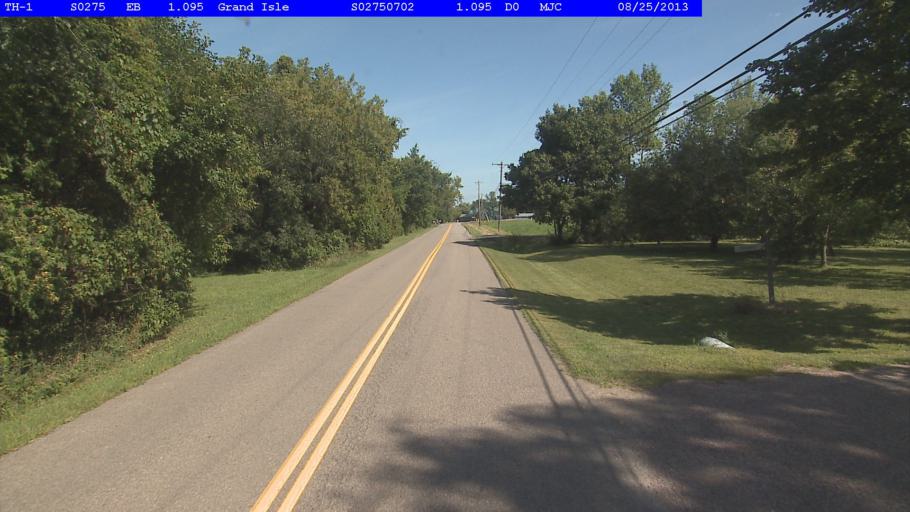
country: US
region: New York
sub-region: Clinton County
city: Cumberland Head
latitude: 44.7161
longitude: -73.3417
